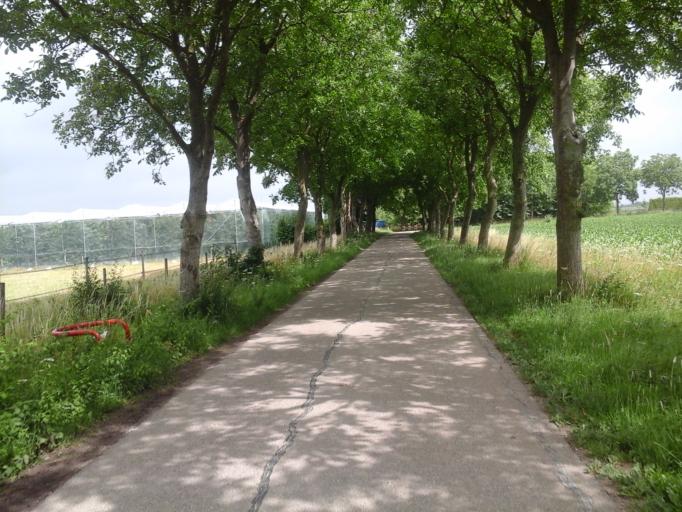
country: NL
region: Gelderland
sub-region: Gemeente Geldermalsen
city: Geldermalsen
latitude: 51.8939
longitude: 5.2511
